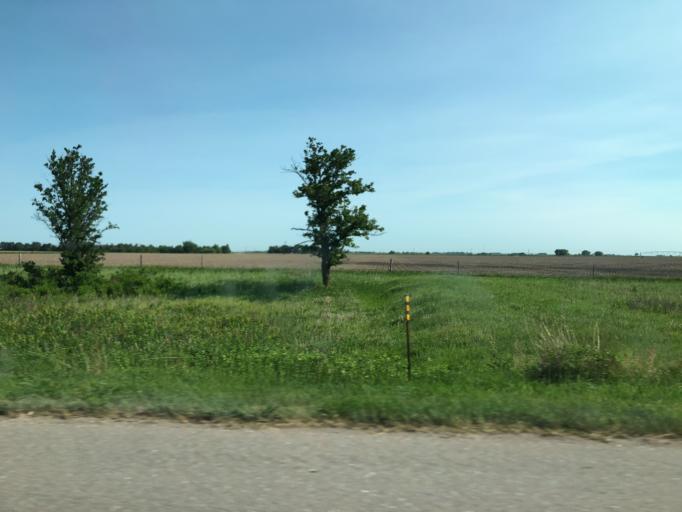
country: US
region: Nebraska
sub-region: Seward County
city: Seward
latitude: 40.8222
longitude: -97.1623
